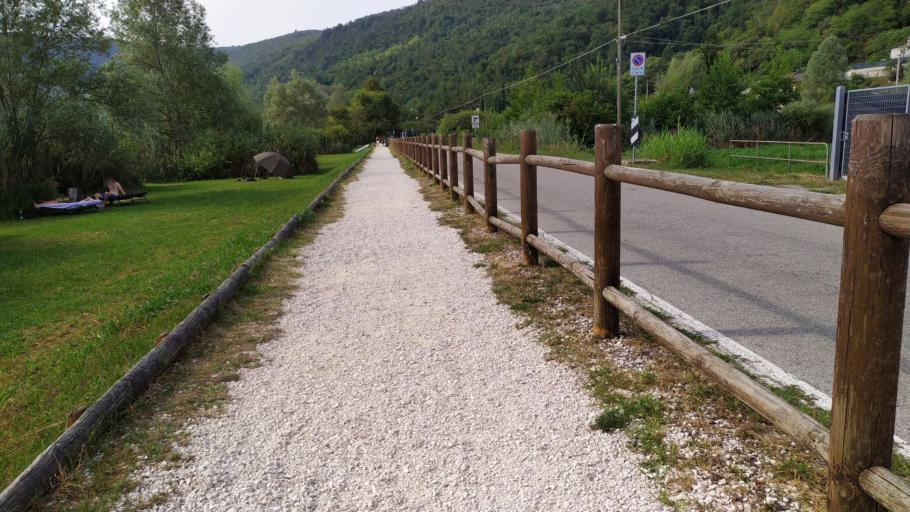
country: IT
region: Veneto
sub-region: Provincia di Vicenza
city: Arcugnano-Torri
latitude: 45.4720
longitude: 11.5412
